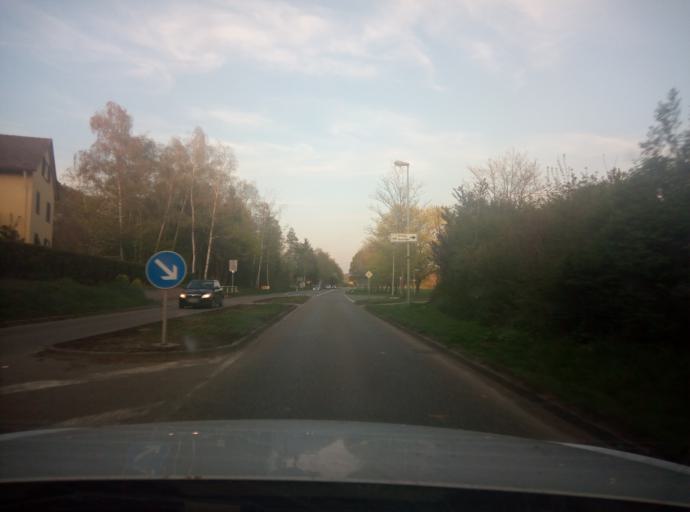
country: DE
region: Baden-Wuerttemberg
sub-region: Tuebingen Region
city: Tuebingen
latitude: 48.5019
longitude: 9.0041
